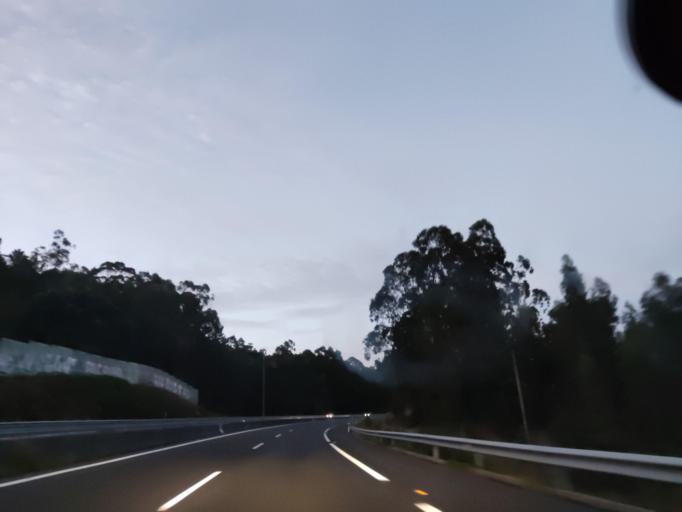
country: ES
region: Galicia
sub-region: Provincia da Coruna
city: Boiro
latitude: 42.6194
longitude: -8.9507
